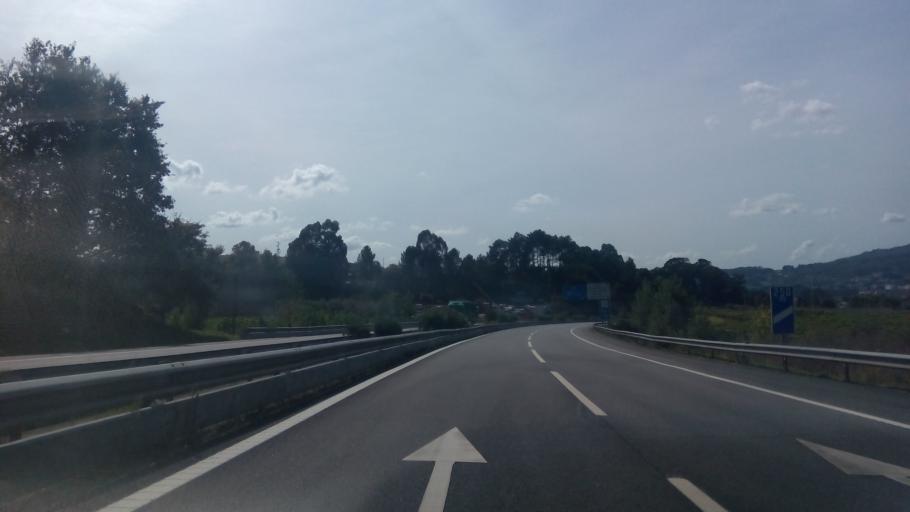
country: PT
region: Porto
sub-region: Penafiel
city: Penafiel
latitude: 41.2030
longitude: -8.3029
